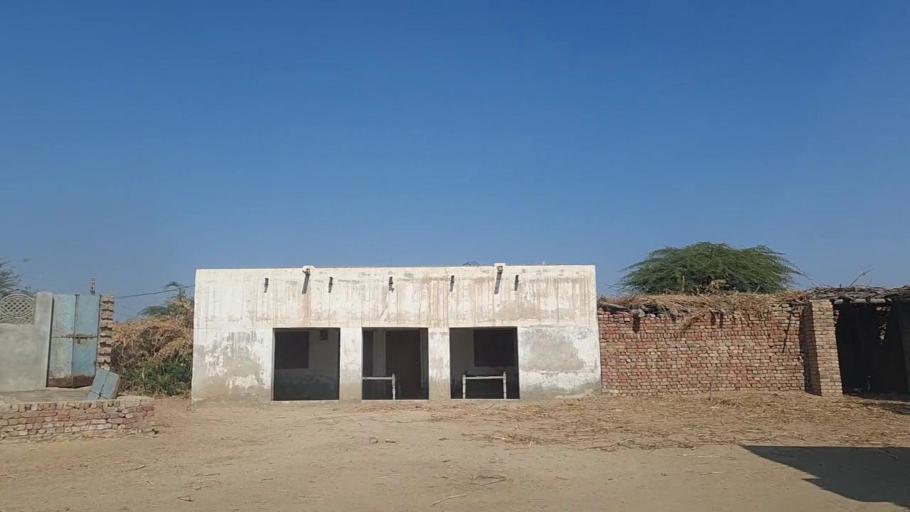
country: PK
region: Sindh
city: Digri
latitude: 25.1722
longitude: 69.1403
